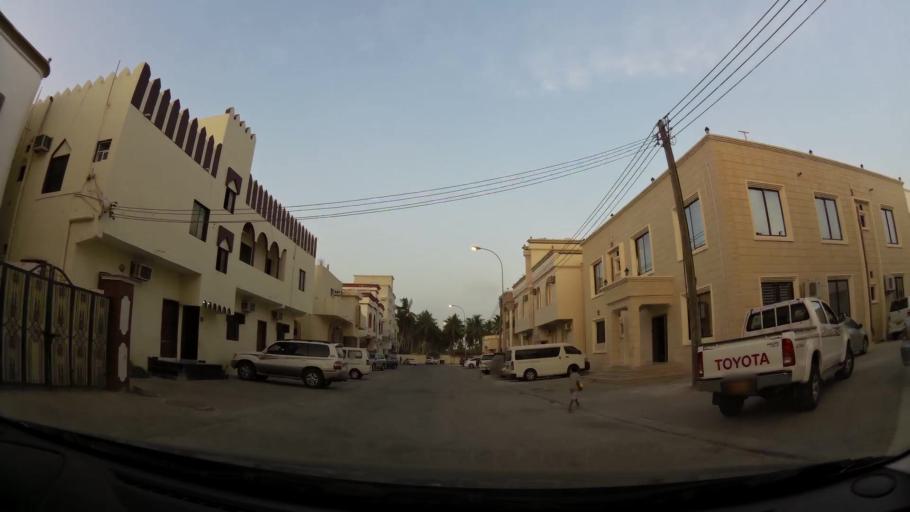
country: OM
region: Zufar
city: Salalah
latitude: 17.0214
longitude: 54.1277
